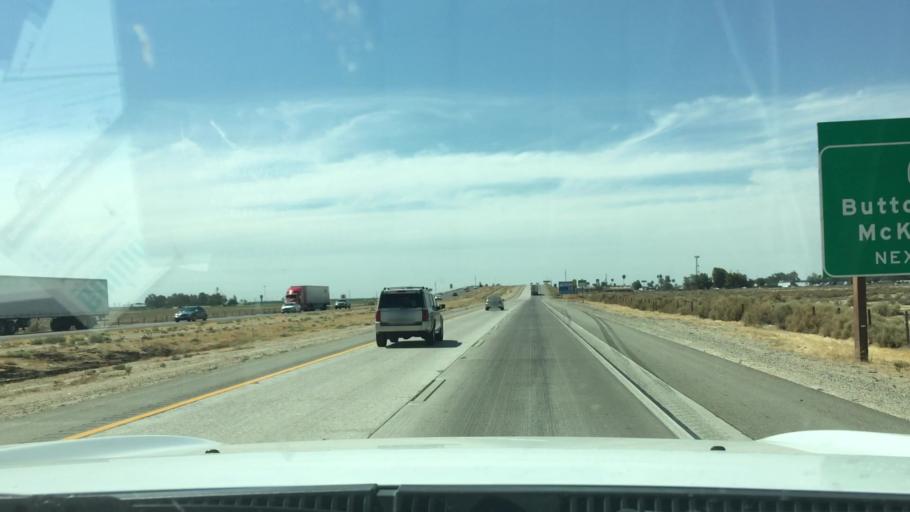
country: US
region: California
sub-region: Kern County
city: Buttonwillow
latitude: 35.3936
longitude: -119.3896
